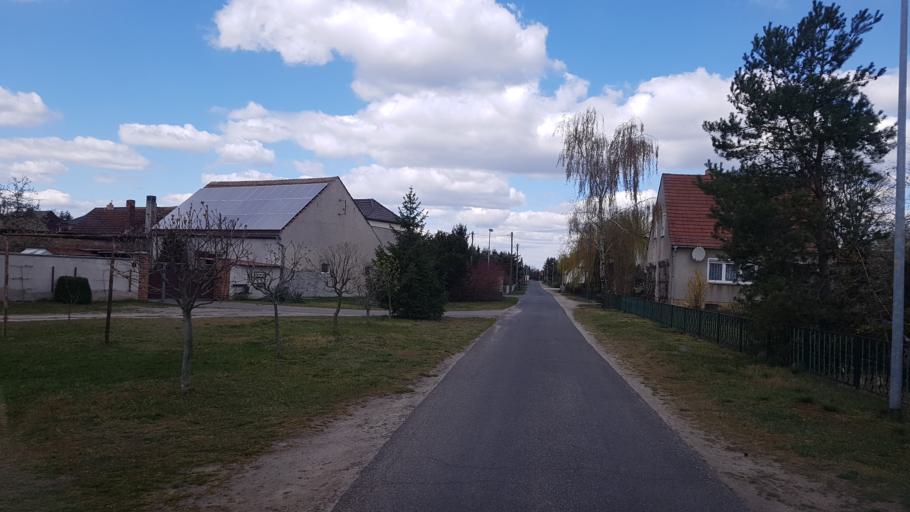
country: DE
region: Brandenburg
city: Sonnewalde
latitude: 51.6842
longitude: 13.6514
